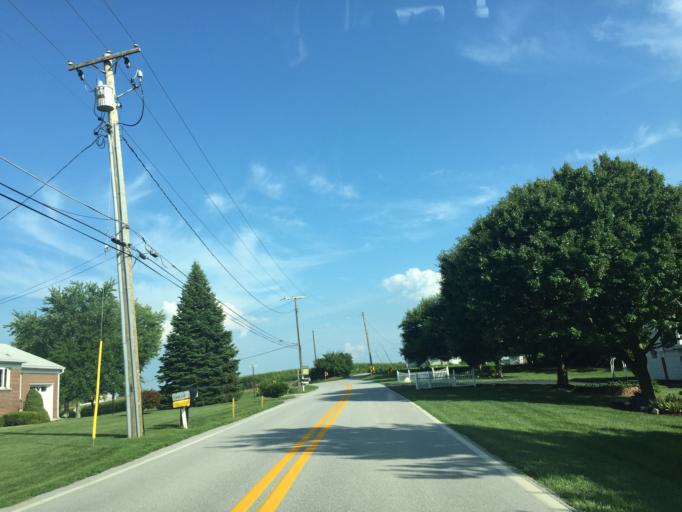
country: US
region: Maryland
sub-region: Carroll County
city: Manchester
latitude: 39.6508
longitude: -76.8467
